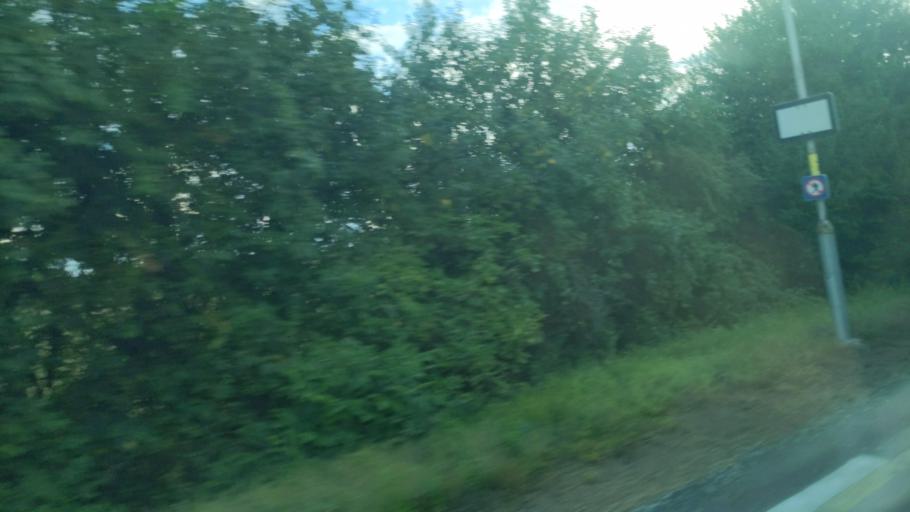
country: CZ
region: Central Bohemia
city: Uvaly
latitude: 50.0771
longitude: 14.7718
